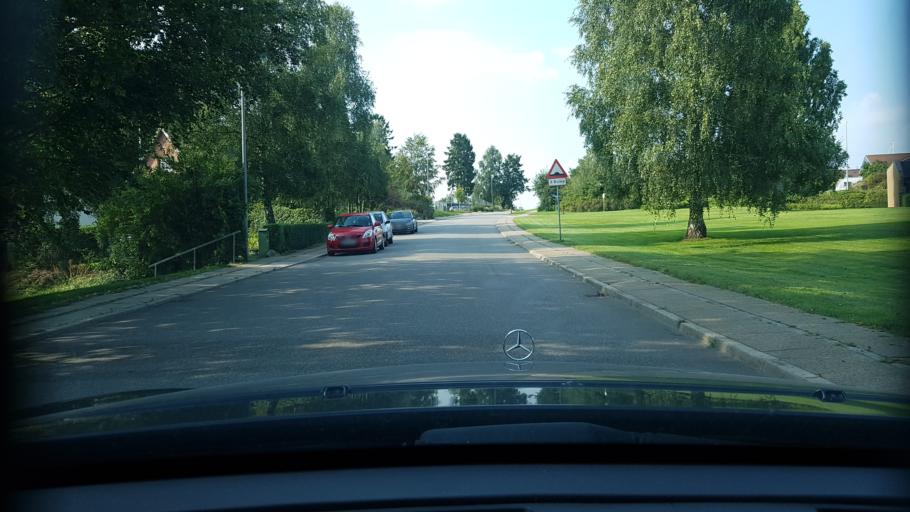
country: DK
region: North Denmark
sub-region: Mariagerfjord Kommune
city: Hadsund
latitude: 56.7235
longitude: 10.1178
